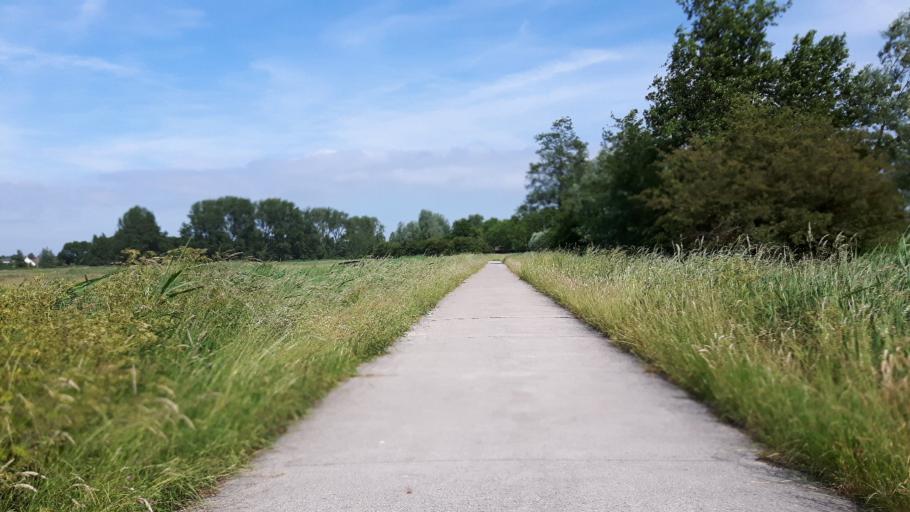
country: NL
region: North Holland
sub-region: Gemeente Uithoorn
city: Uithoorn
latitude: 52.2275
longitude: 4.8086
